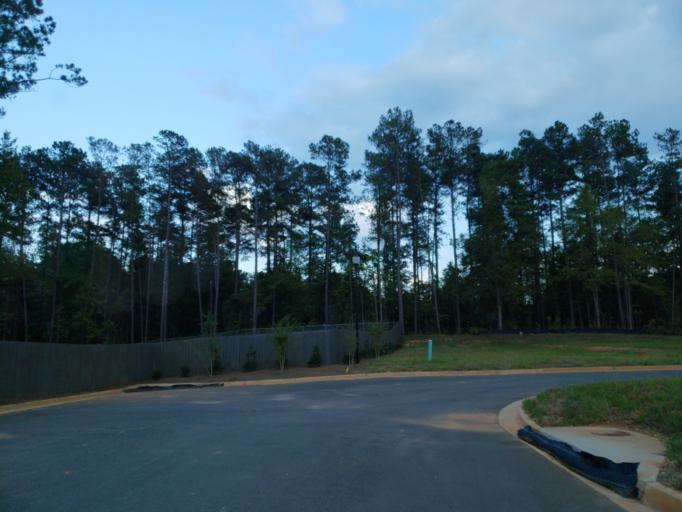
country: US
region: Georgia
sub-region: Cobb County
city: Powder Springs
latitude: 33.8788
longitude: -84.6204
